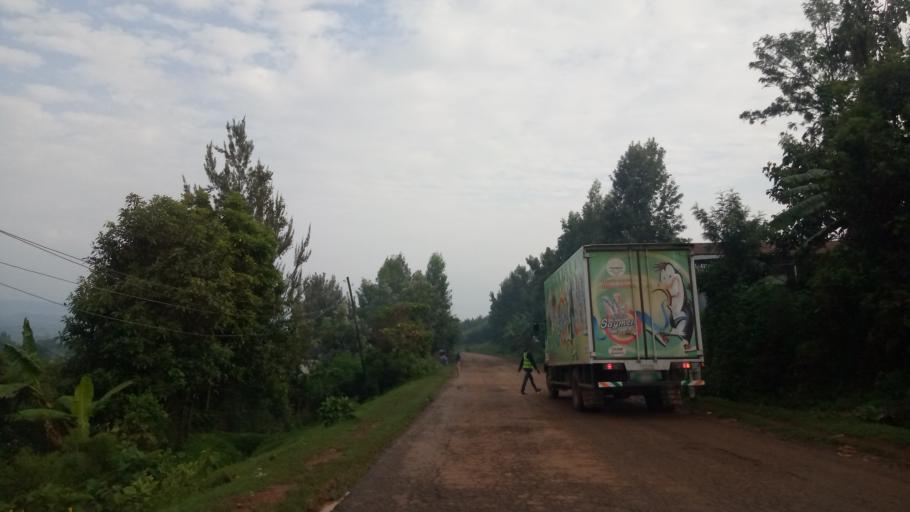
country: ET
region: Oromiya
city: Agaro
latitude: 7.7918
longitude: 36.7257
